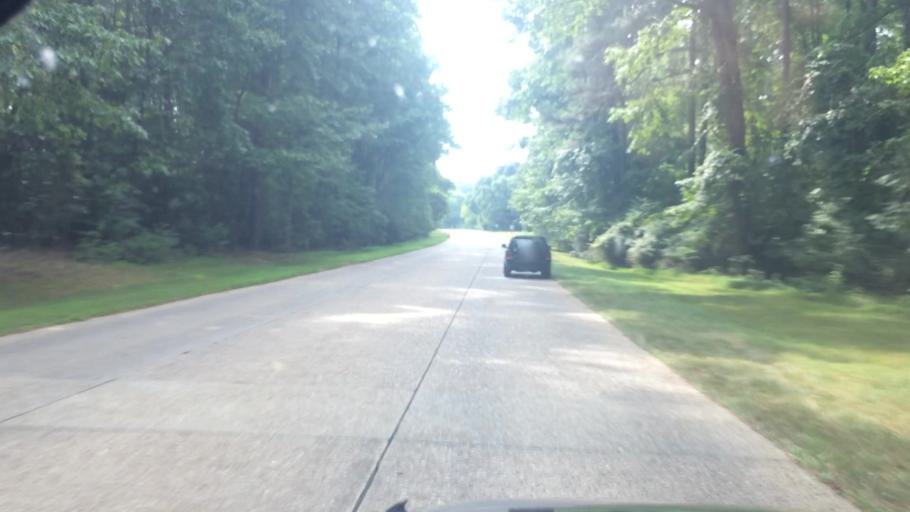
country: US
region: Virginia
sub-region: James City County
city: Williamsburg
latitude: 37.2187
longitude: -76.7622
